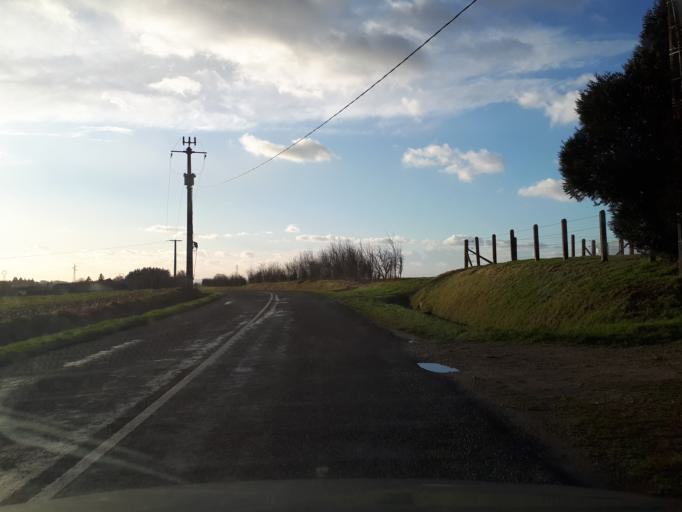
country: FR
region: Pays de la Loire
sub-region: Departement de la Sarthe
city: Mamers
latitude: 48.3359
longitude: 0.3294
